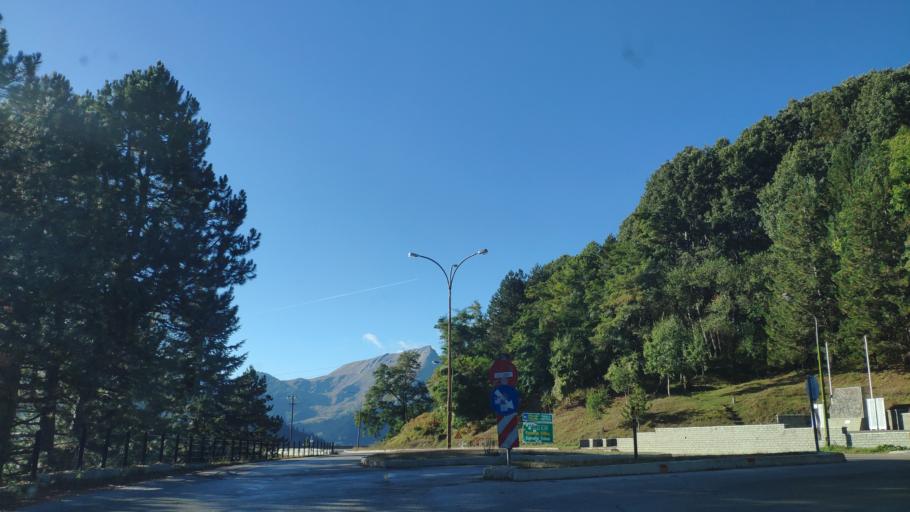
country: GR
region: Epirus
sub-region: Nomos Ioanninon
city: Metsovo
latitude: 39.7676
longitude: 21.1768
